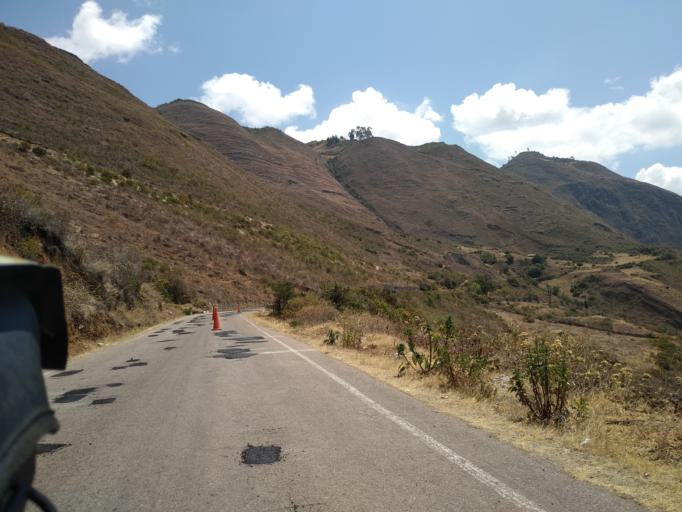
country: PE
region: Cajamarca
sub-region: Provincia de Celendin
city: Celendin
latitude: -6.8839
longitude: -78.1018
